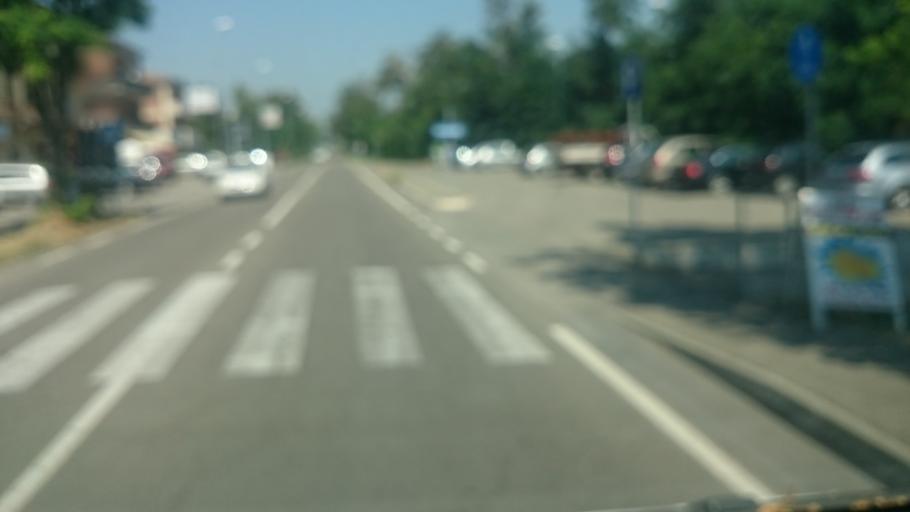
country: IT
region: Emilia-Romagna
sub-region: Provincia di Reggio Emilia
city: Scandiano
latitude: 44.6015
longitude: 10.6916
